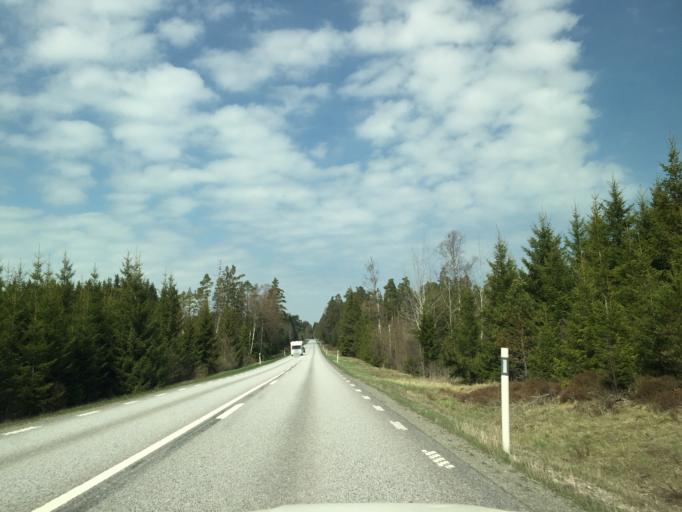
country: SE
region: Vaestra Goetaland
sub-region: Bengtsfors Kommun
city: Dals Langed
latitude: 58.8142
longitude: 12.1448
